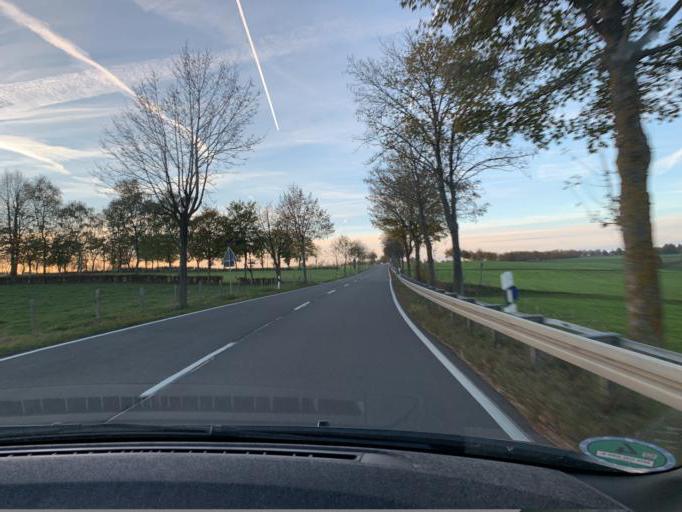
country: DE
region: North Rhine-Westphalia
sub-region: Regierungsbezirk Koln
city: Simmerath
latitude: 50.5948
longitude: 6.3540
